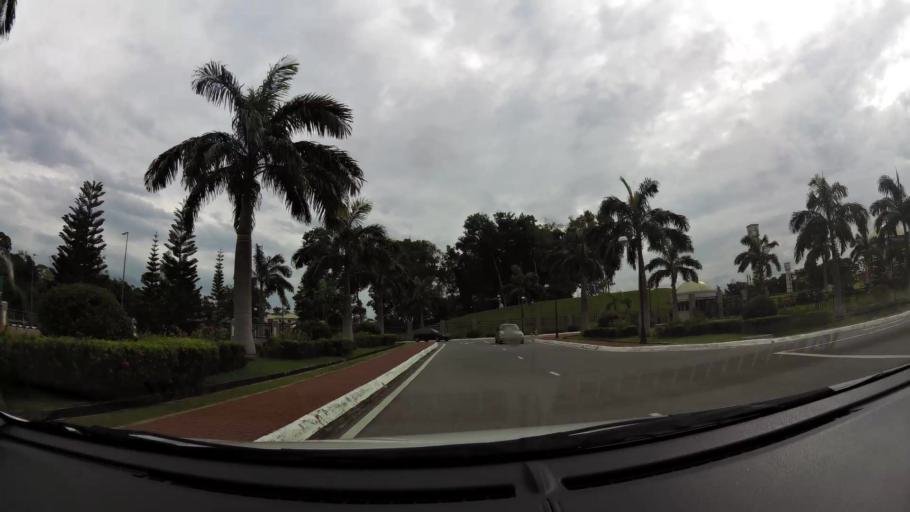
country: BN
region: Brunei and Muara
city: Bandar Seri Begawan
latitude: 4.9206
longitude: 114.9358
